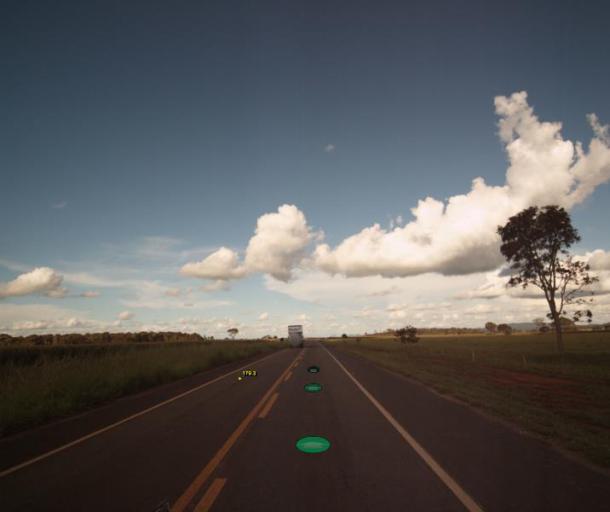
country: BR
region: Goias
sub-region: Itaberai
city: Itaberai
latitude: -15.9852
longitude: -49.7005
